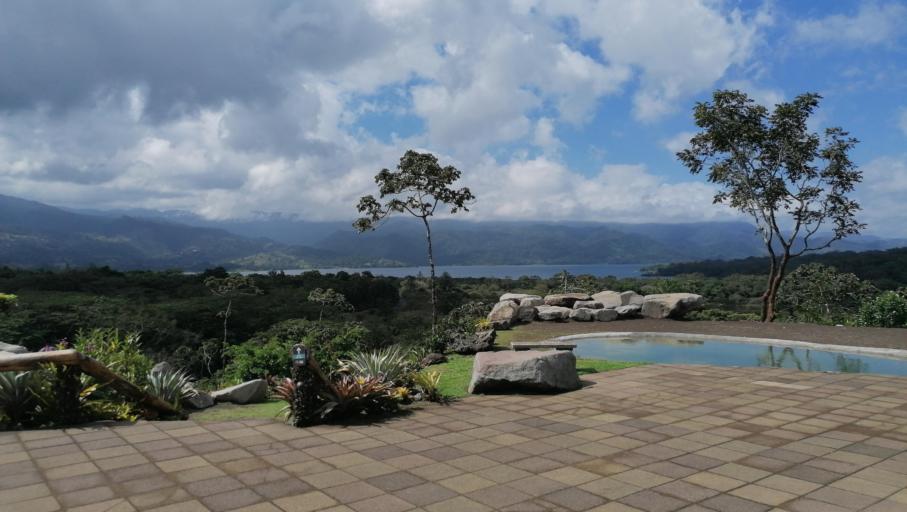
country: CR
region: Alajuela
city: La Fortuna
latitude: 10.4674
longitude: -84.7358
